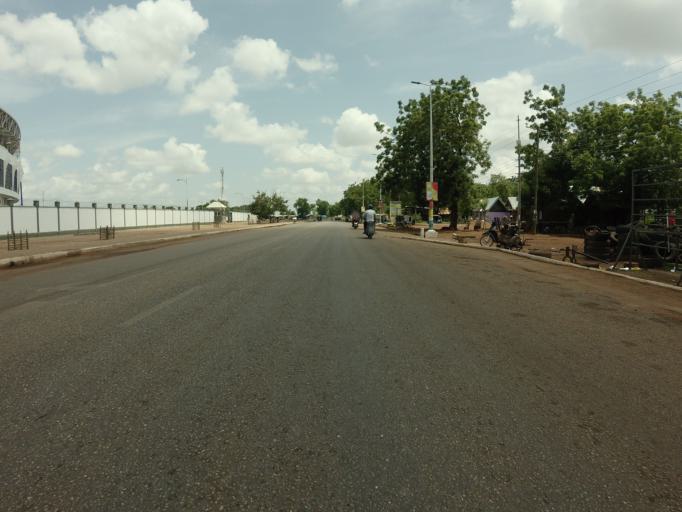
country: GH
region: Northern
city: Tamale
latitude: 9.4114
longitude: -0.8625
